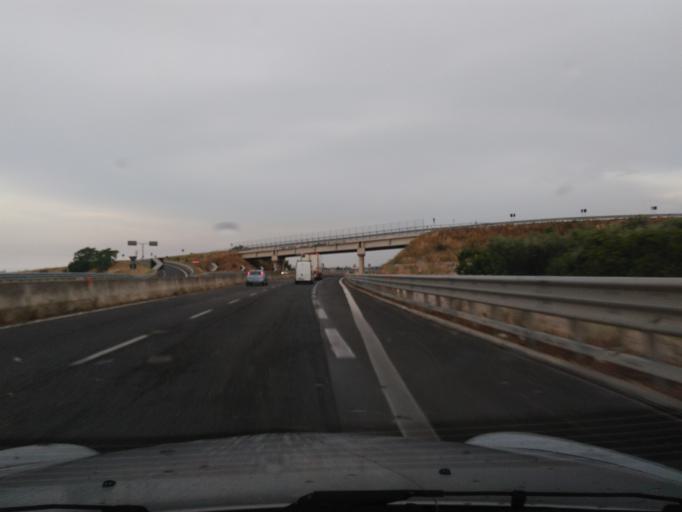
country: IT
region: Apulia
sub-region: Provincia di Bari
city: Molfetta
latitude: 41.1883
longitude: 16.6151
